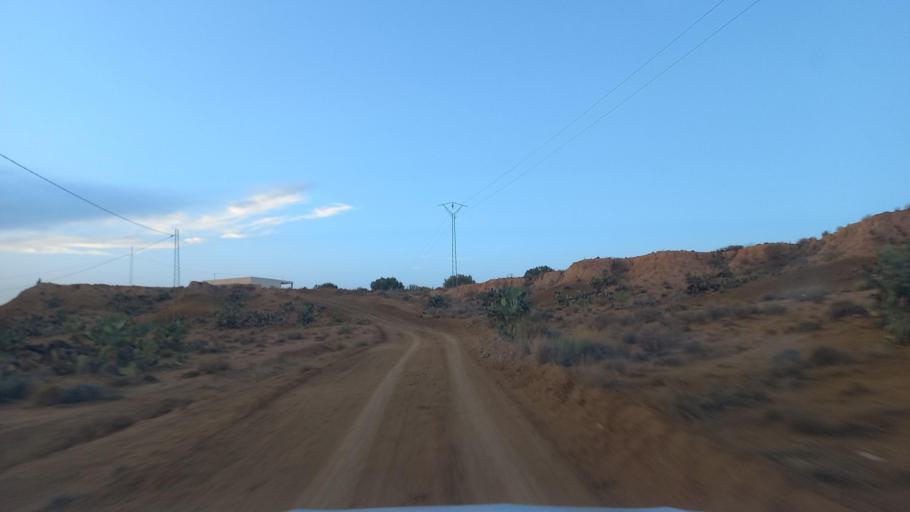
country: TN
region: Al Qasrayn
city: Kasserine
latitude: 35.2097
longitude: 9.0513
